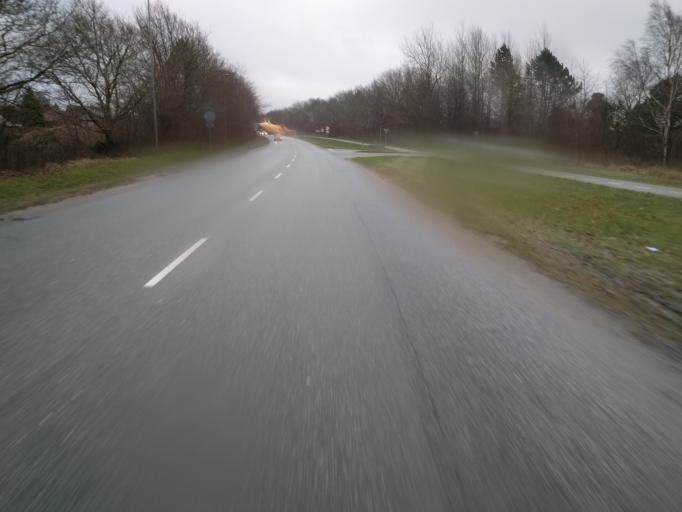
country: DK
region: Central Jutland
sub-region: Viborg Kommune
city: Viborg
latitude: 56.4563
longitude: 9.4446
